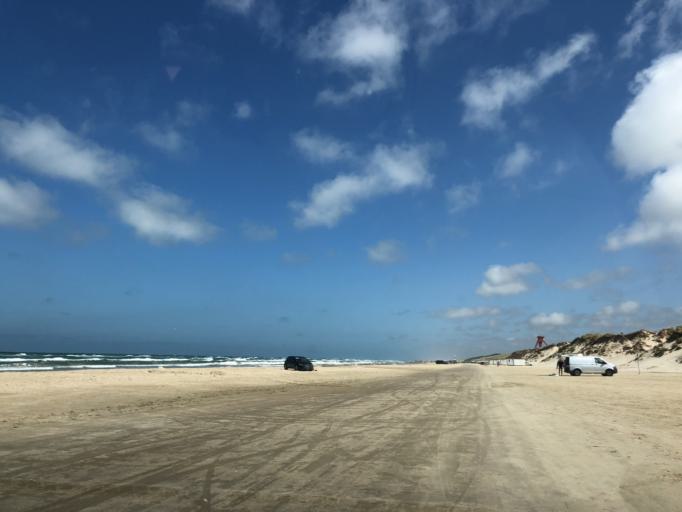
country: DK
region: North Denmark
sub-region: Jammerbugt Kommune
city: Pandrup
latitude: 57.2506
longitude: 9.5738
